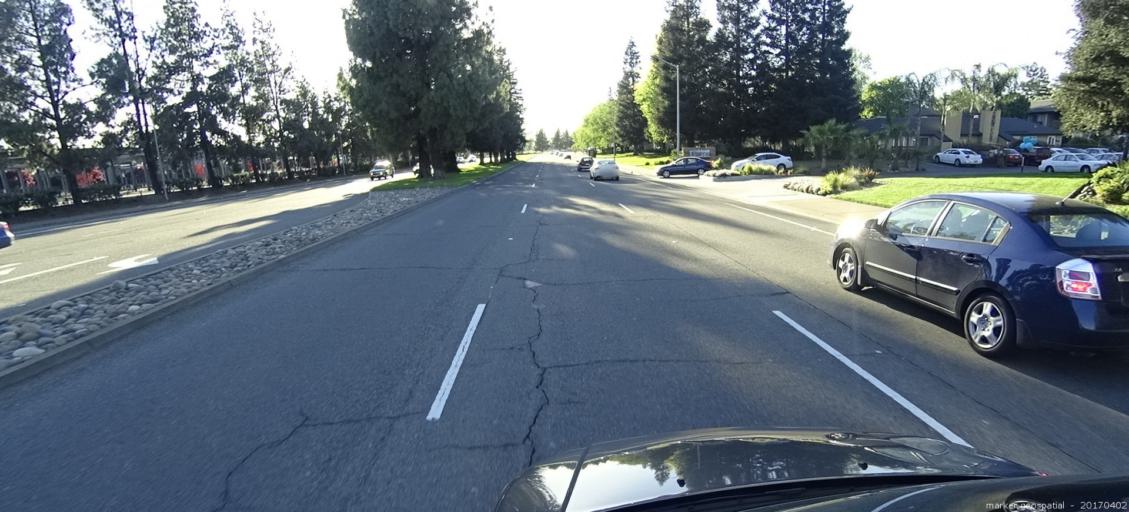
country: US
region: California
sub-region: Sacramento County
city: Arden-Arcade
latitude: 38.5956
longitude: -121.4356
